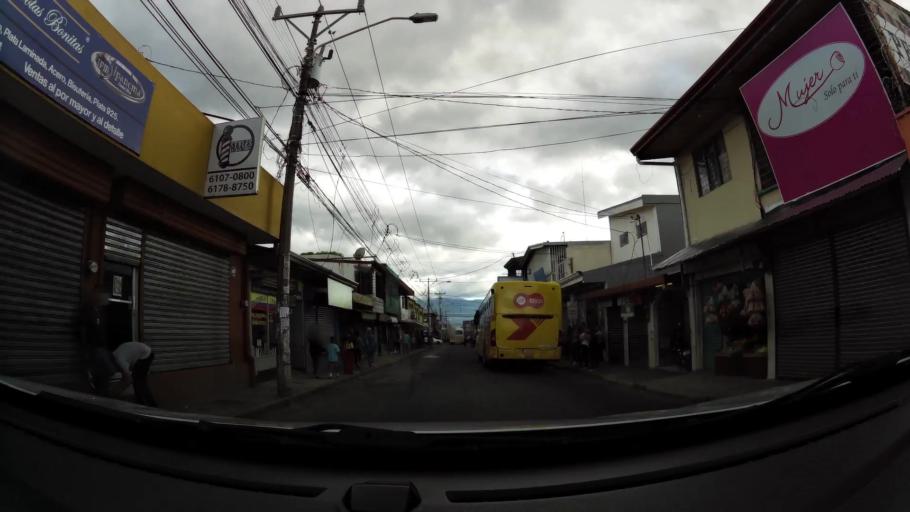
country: CR
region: Alajuela
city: Alajuela
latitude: 10.0177
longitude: -84.2173
